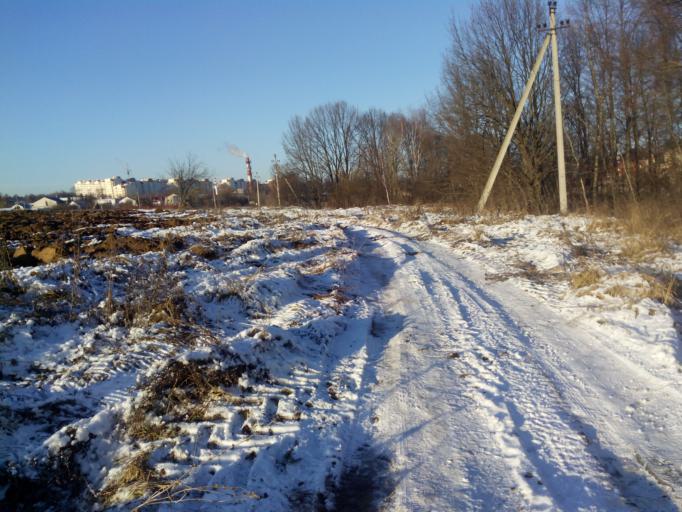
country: RU
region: Moskovskaya
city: Yakovlevskoye
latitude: 55.4956
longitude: 37.9534
